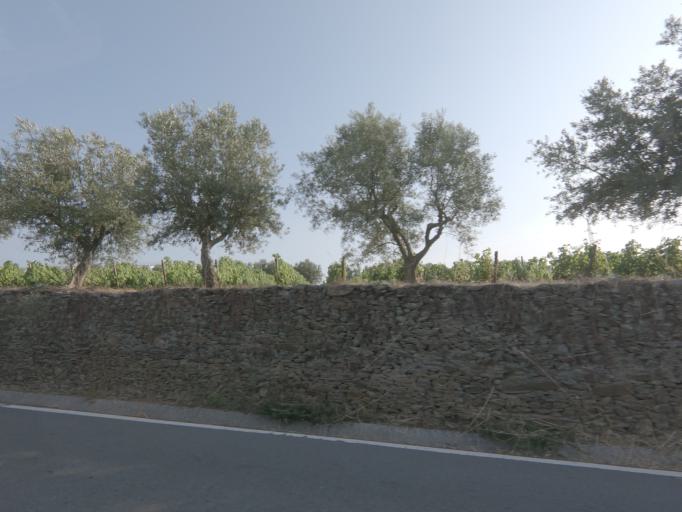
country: PT
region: Viseu
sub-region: Tabuaco
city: Tabuaco
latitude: 41.1382
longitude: -7.5997
